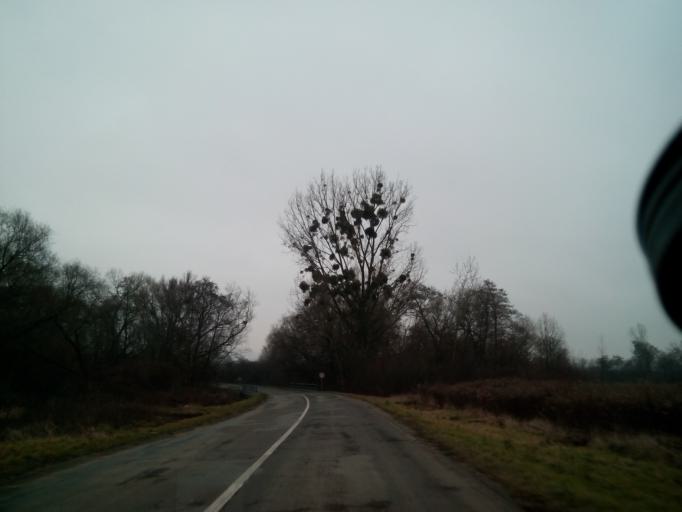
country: SK
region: Kosicky
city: Kosice
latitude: 48.7221
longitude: 21.4372
